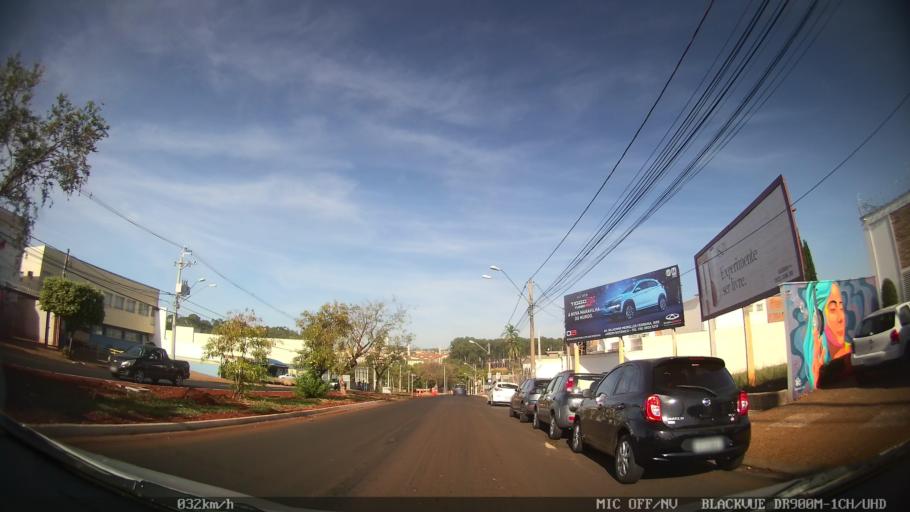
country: BR
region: Sao Paulo
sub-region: Ribeirao Preto
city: Ribeirao Preto
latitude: -21.2070
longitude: -47.8228
